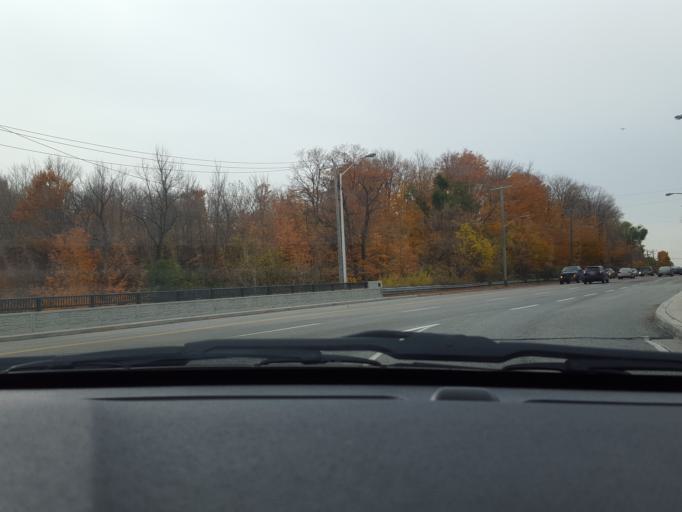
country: CA
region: Ontario
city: Willowdale
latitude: 43.7391
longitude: -79.3343
